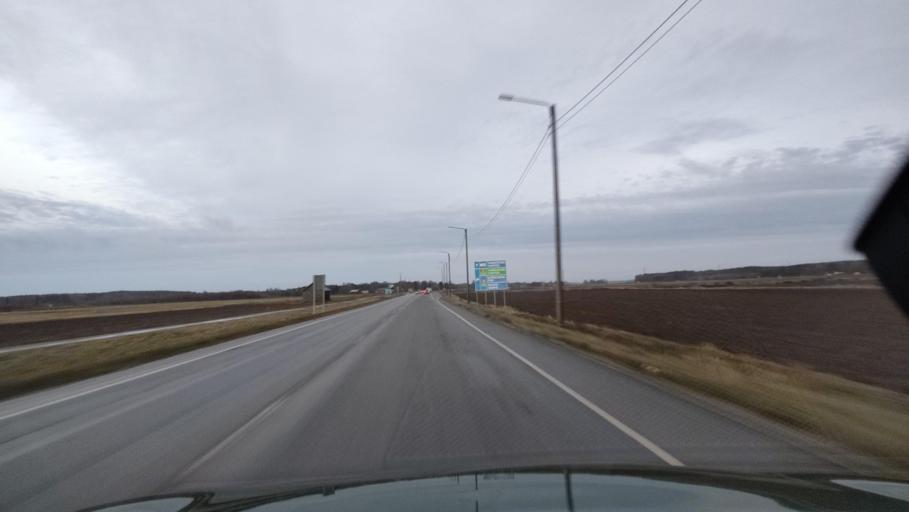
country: FI
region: Ostrobothnia
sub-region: Vaasa
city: Ristinummi
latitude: 63.0368
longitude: 21.7534
